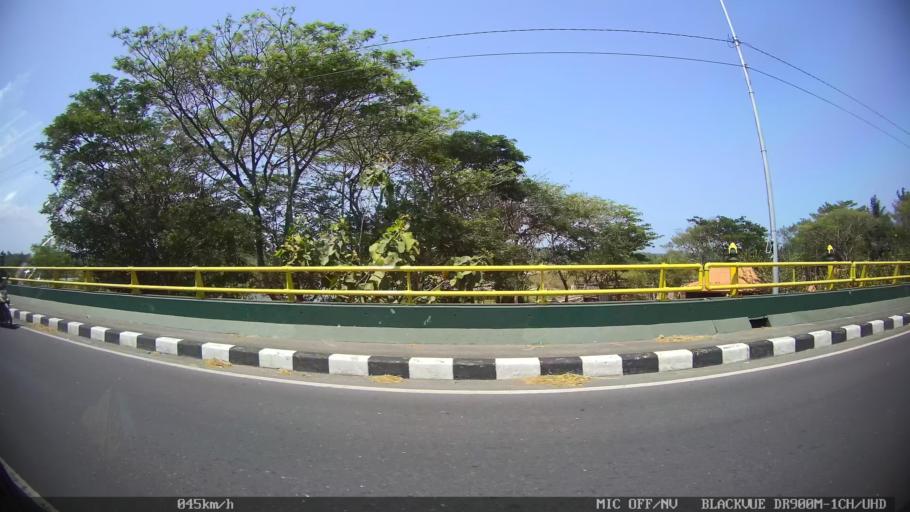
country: ID
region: Daerah Istimewa Yogyakarta
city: Srandakan
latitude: -7.9399
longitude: 110.2404
